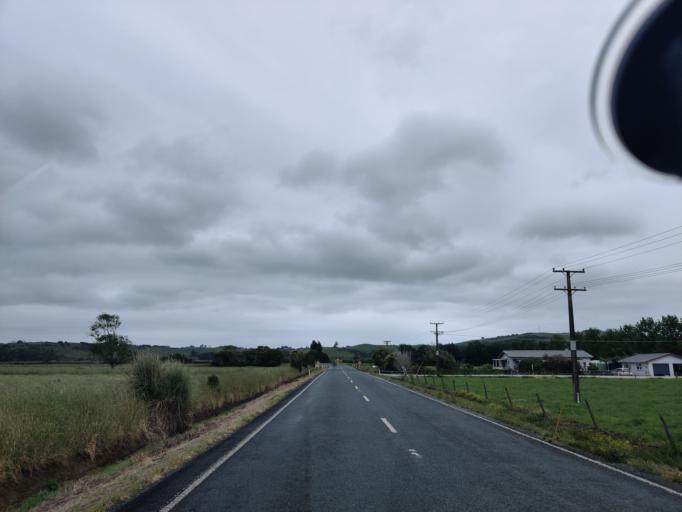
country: NZ
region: Northland
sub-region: Kaipara District
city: Dargaville
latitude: -36.1220
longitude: 174.0917
